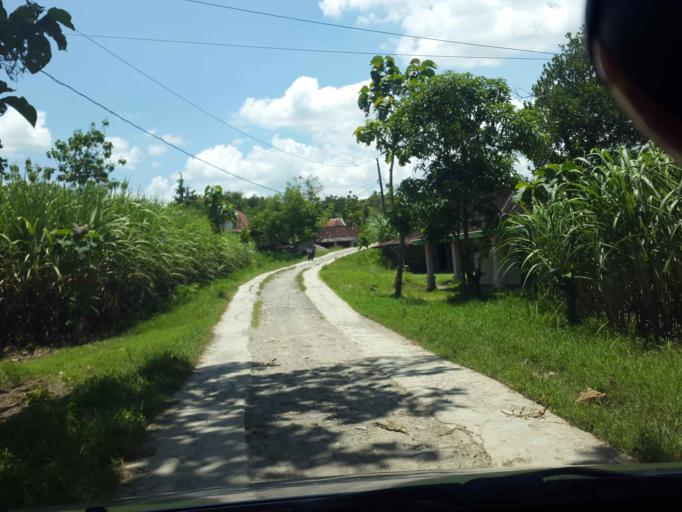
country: ID
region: Central Java
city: Sragen
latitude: -7.2709
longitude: 111.1316
